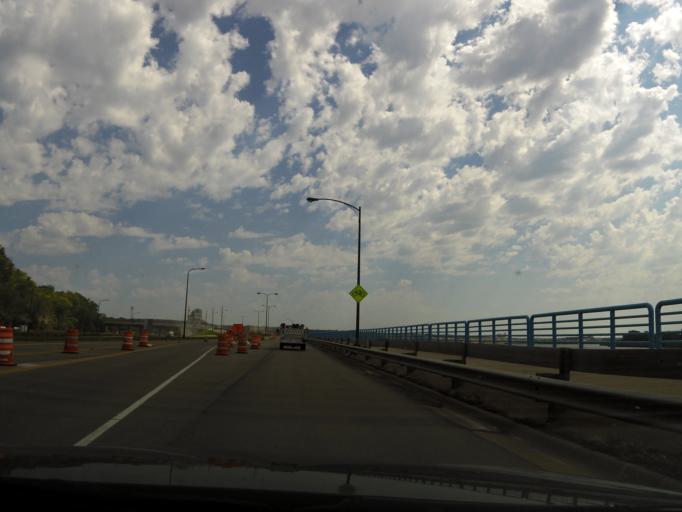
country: US
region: Minnesota
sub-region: Ramsey County
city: Saint Paul
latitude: 44.9451
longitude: -93.0596
